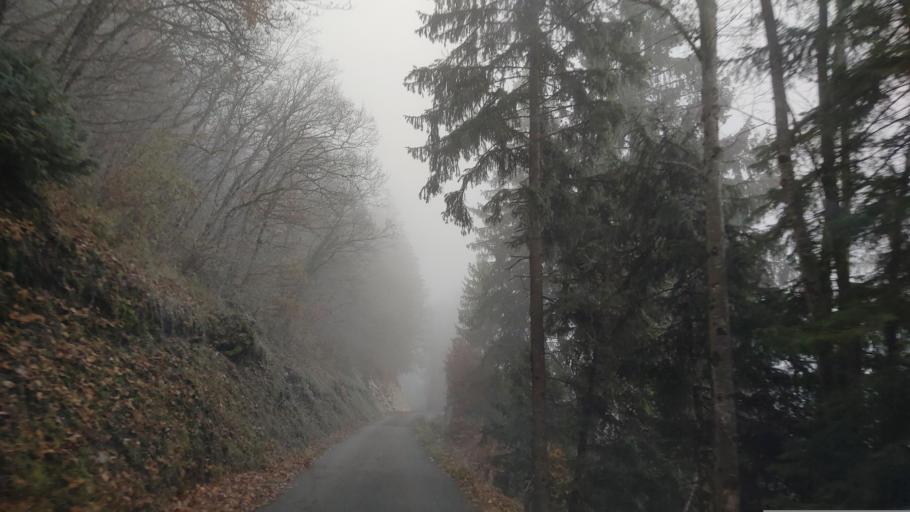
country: FR
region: Rhone-Alpes
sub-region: Departement de la Haute-Savoie
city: Doussard
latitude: 45.6898
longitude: 6.1429
